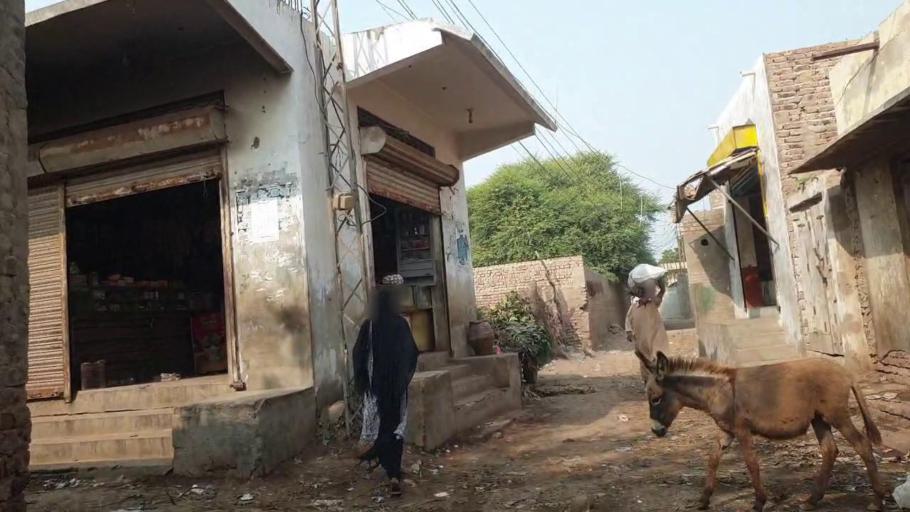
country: PK
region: Sindh
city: Tando Muhammad Khan
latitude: 25.1963
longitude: 68.5661
